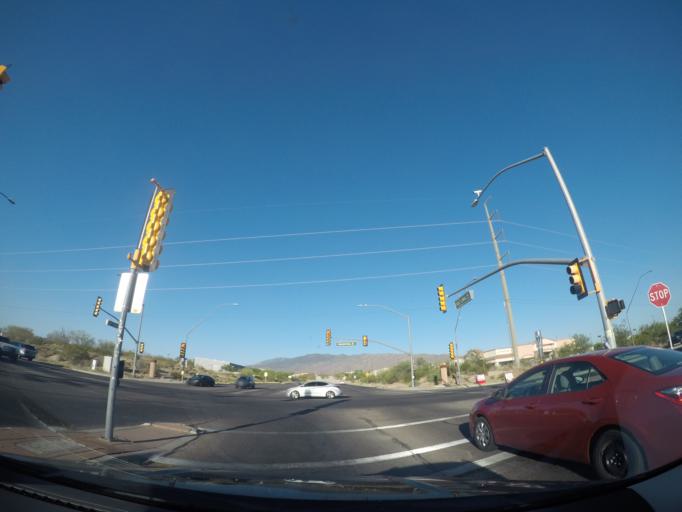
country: US
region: Arizona
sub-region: Pima County
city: Tanque Verde
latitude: 32.1918
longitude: -110.7730
